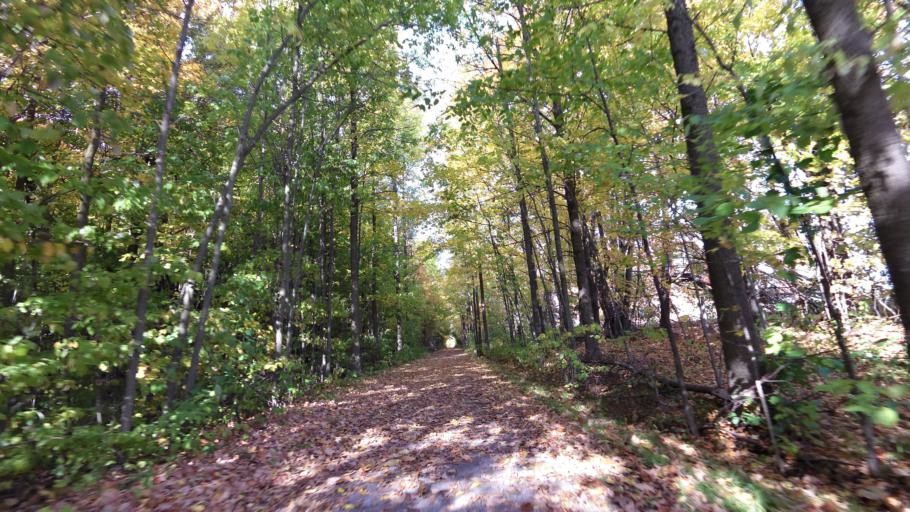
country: CA
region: Ontario
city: Orangeville
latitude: 43.8057
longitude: -80.0333
